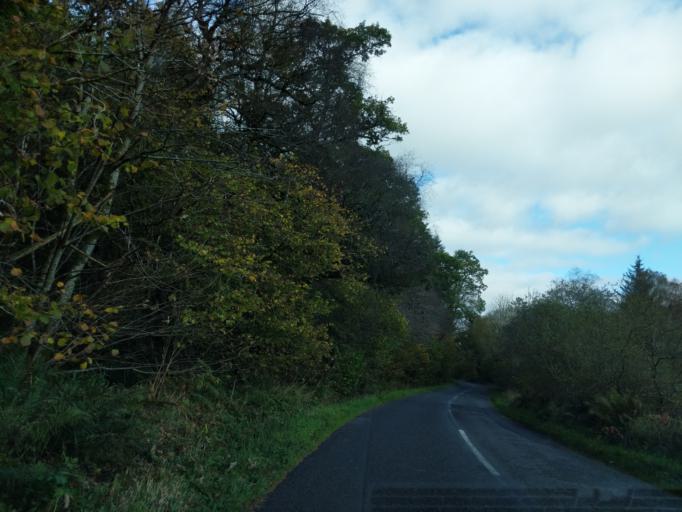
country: GB
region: Scotland
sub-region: Dumfries and Galloway
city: Thornhill
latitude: 55.1742
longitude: -3.9492
